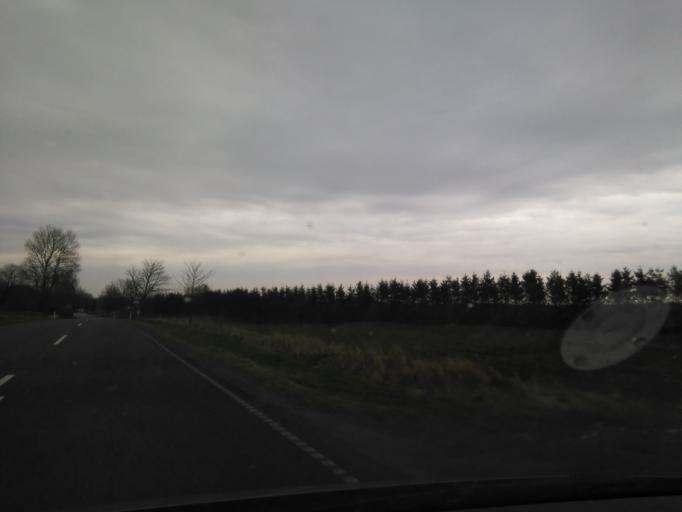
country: DK
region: North Denmark
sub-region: Mariagerfjord Kommune
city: Mariager
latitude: 56.6917
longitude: 9.9674
